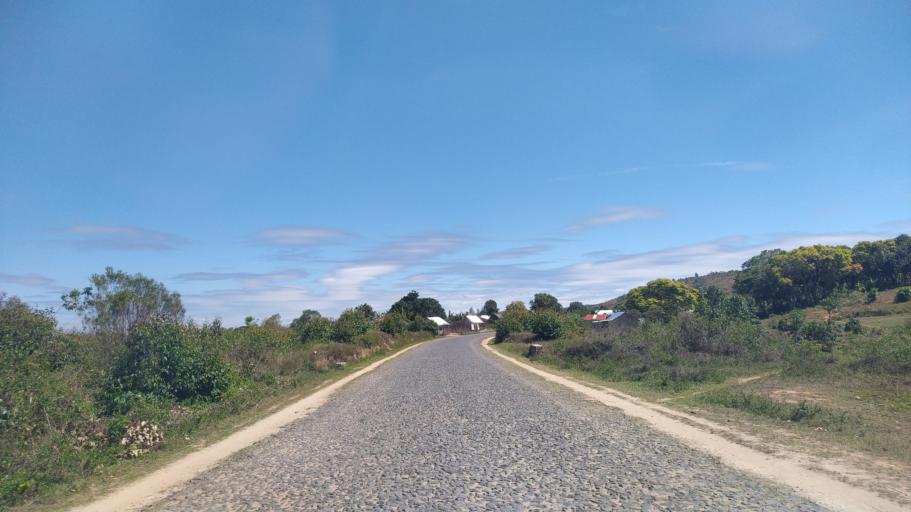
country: MG
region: Alaotra Mangoro
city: Moramanga
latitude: -18.7542
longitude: 48.2595
